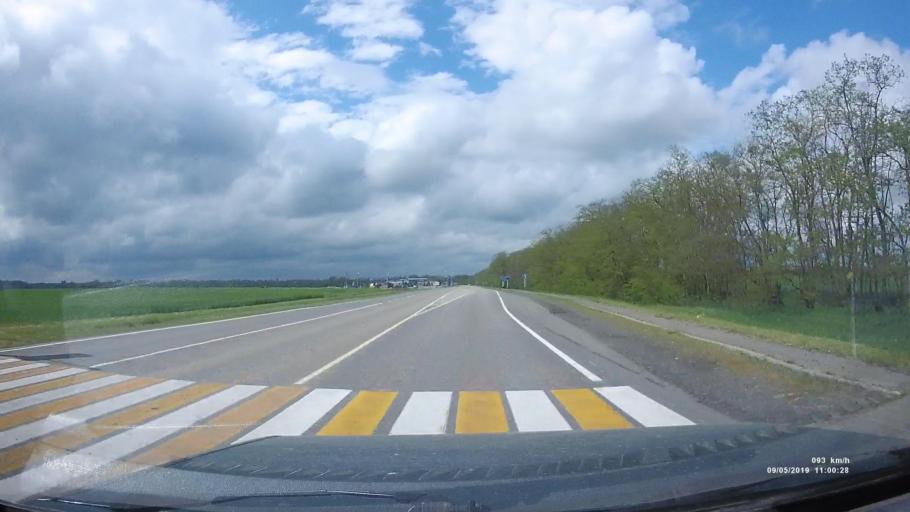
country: RU
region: Rostov
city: Peshkovo
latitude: 46.8530
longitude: 39.2192
